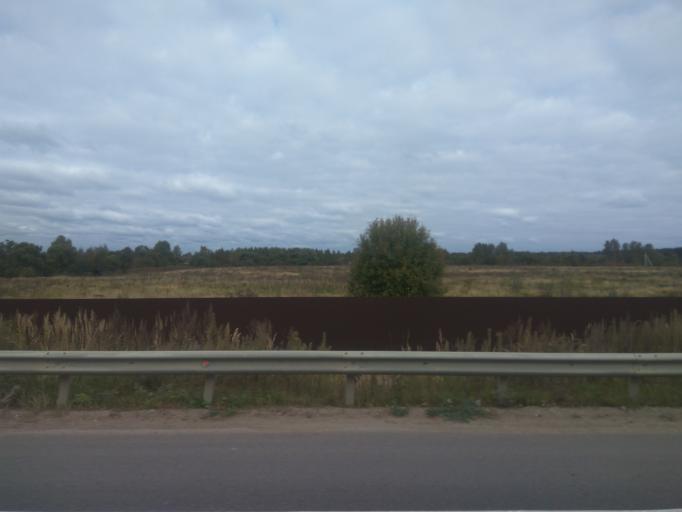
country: RU
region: Moskovskaya
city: Krasnoarmeysk
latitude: 56.0210
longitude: 38.1714
